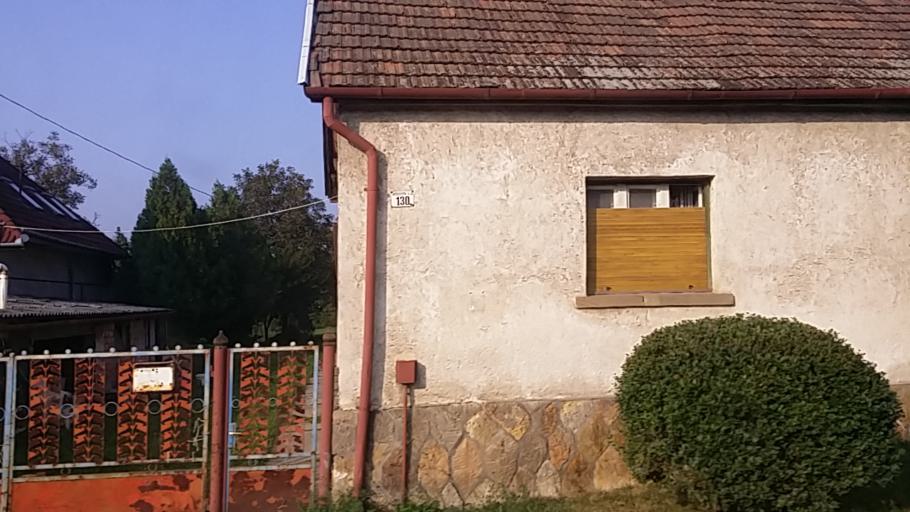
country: HU
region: Pest
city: Pilisszanto
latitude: 47.6722
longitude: 18.8865
